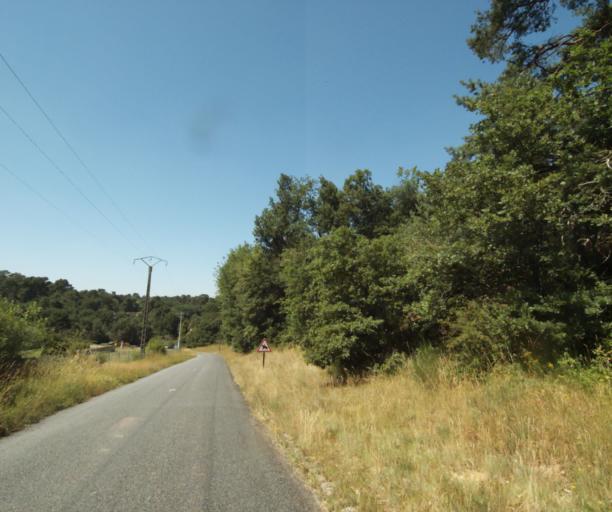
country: FR
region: Ile-de-France
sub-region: Departement de Seine-et-Marne
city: Noisy-sur-Ecole
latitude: 48.3165
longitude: 2.5008
